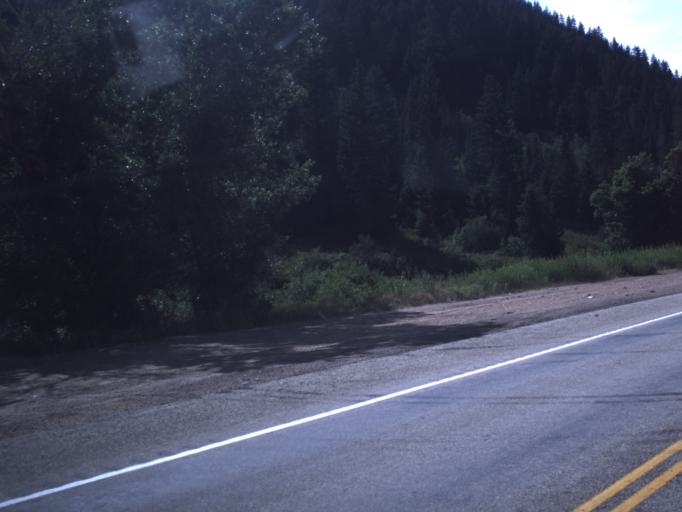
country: US
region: Utah
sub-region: Wasatch County
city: Heber
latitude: 40.3504
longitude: -111.2726
